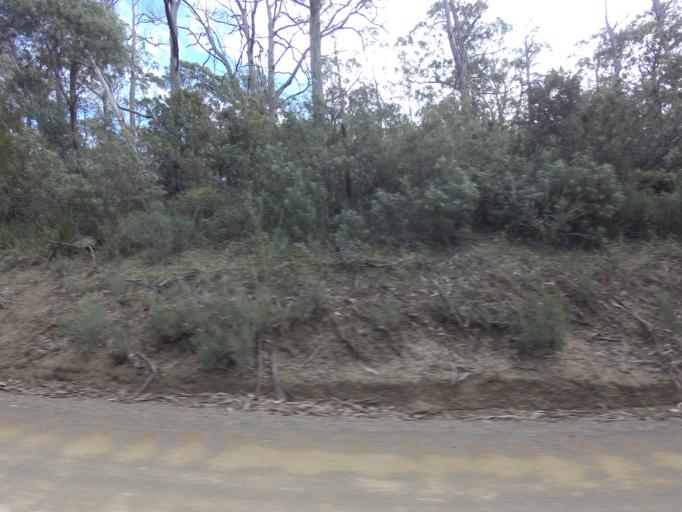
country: AU
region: Tasmania
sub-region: Clarence
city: Sandford
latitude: -43.0942
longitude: 147.7234
